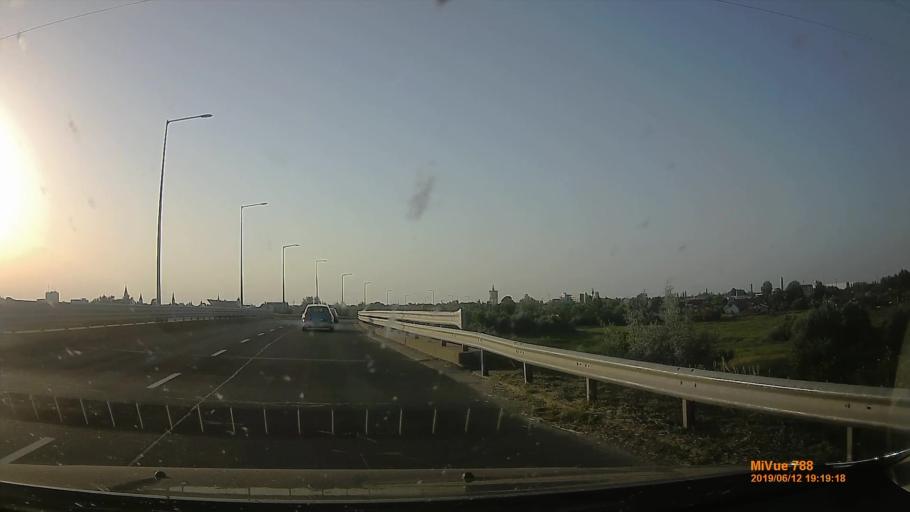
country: HU
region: Bacs-Kiskun
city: Kecskemet
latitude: 46.8970
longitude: 19.7044
